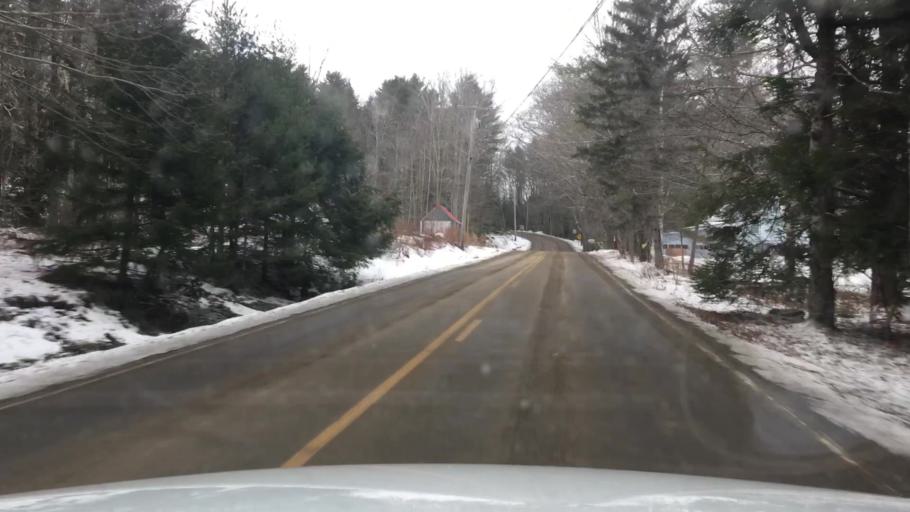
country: US
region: Maine
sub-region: Waldo County
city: Lincolnville
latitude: 44.2852
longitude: -69.0156
